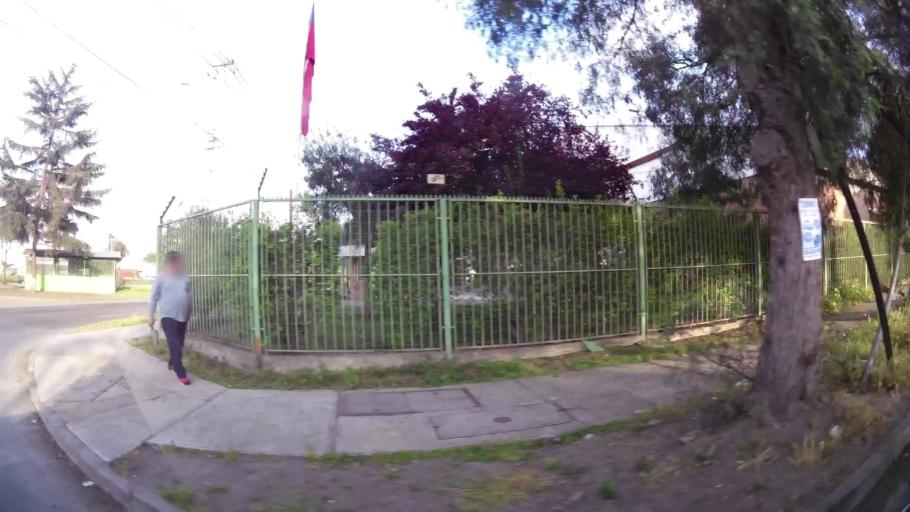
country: CL
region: Santiago Metropolitan
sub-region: Provincia de Maipo
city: San Bernardo
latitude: -33.5576
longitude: -70.7176
